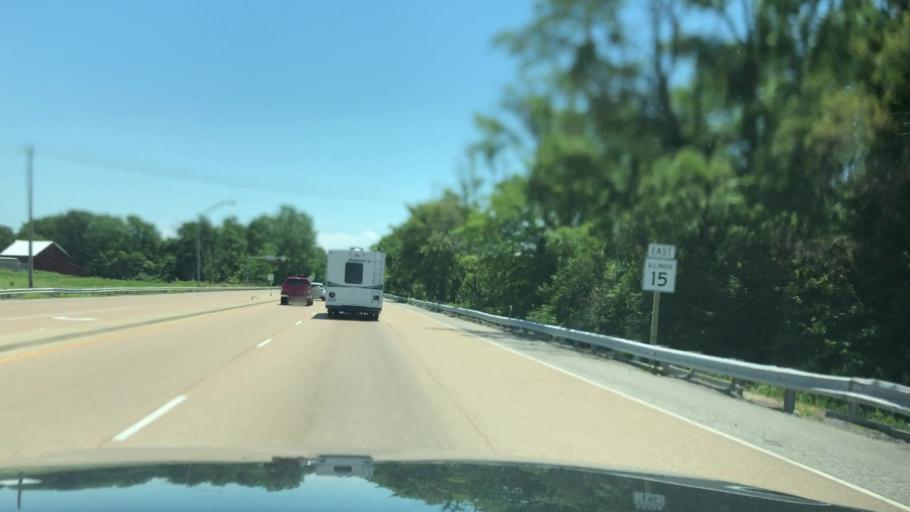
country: US
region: Illinois
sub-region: Saint Clair County
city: Alorton
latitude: 38.5612
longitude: -90.0844
